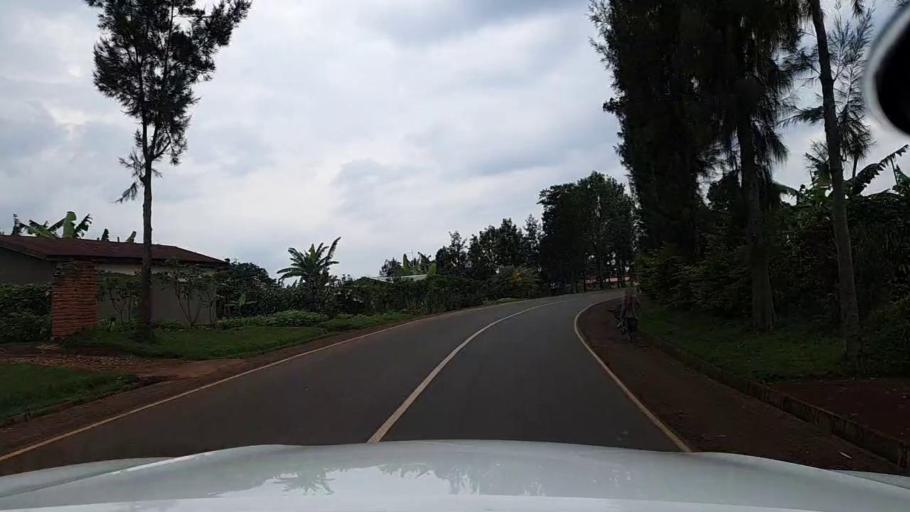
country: RW
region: Western Province
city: Cyangugu
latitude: -2.5955
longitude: 28.9320
